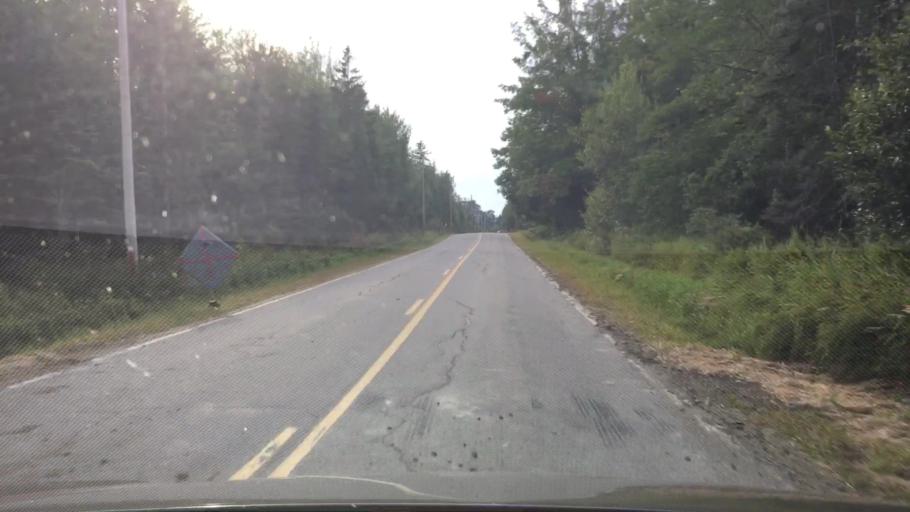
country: US
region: Maine
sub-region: Hancock County
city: Penobscot
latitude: 44.4734
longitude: -68.7724
